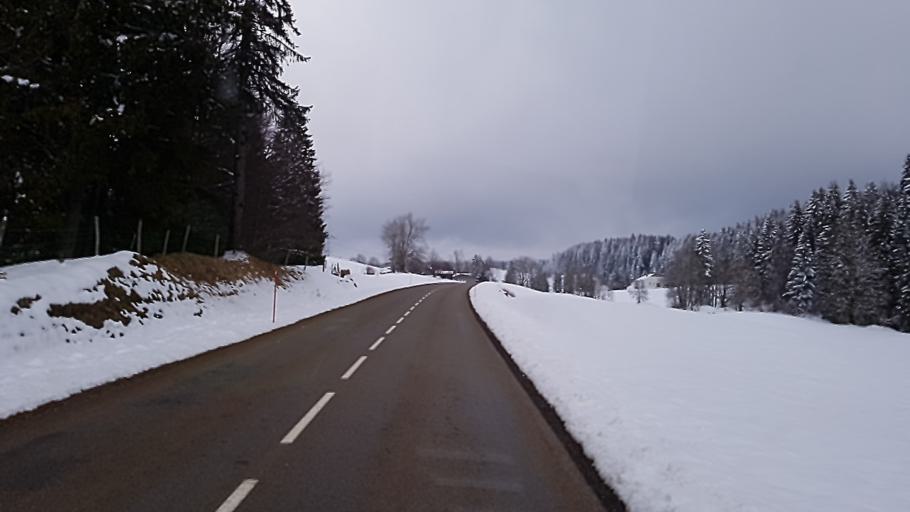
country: FR
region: Franche-Comte
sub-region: Departement du Jura
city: Longchaumois
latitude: 46.3893
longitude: 5.9420
